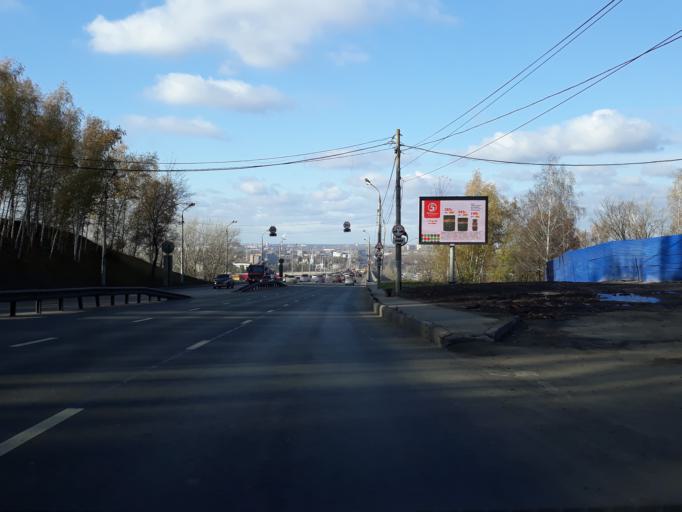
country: RU
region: Nizjnij Novgorod
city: Nizhniy Novgorod
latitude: 56.2464
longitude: 43.9548
